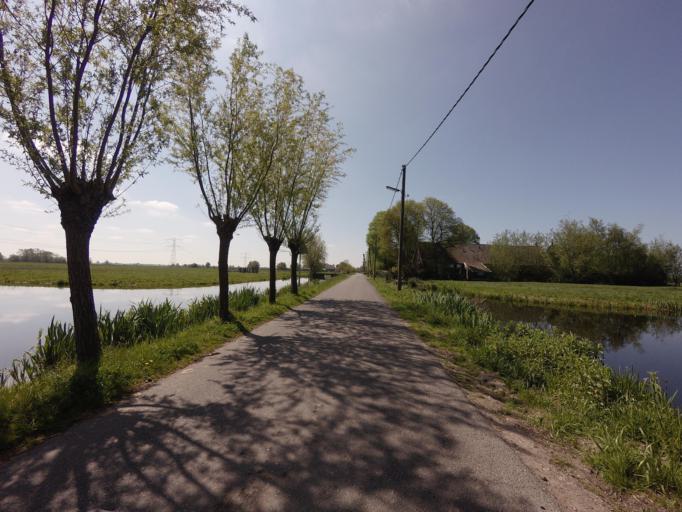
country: NL
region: South Holland
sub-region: Gemeente Gouda
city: Gouda
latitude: 51.9757
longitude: 4.7090
